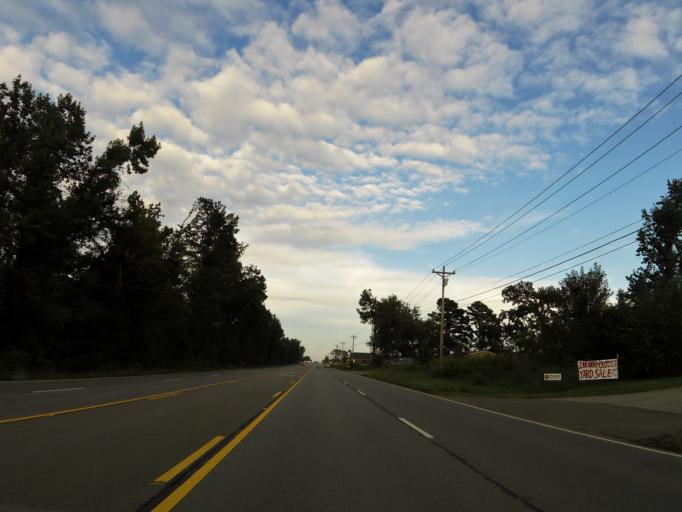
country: US
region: Alabama
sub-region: Lauderdale County
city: Rogersville
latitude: 34.8015
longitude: -87.1706
